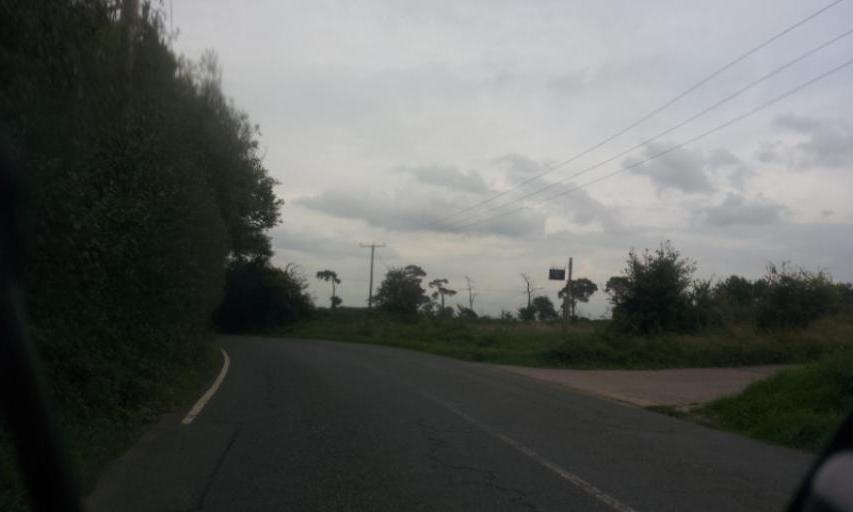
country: GB
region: England
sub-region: Kent
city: East Peckham
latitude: 51.2065
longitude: 0.3669
